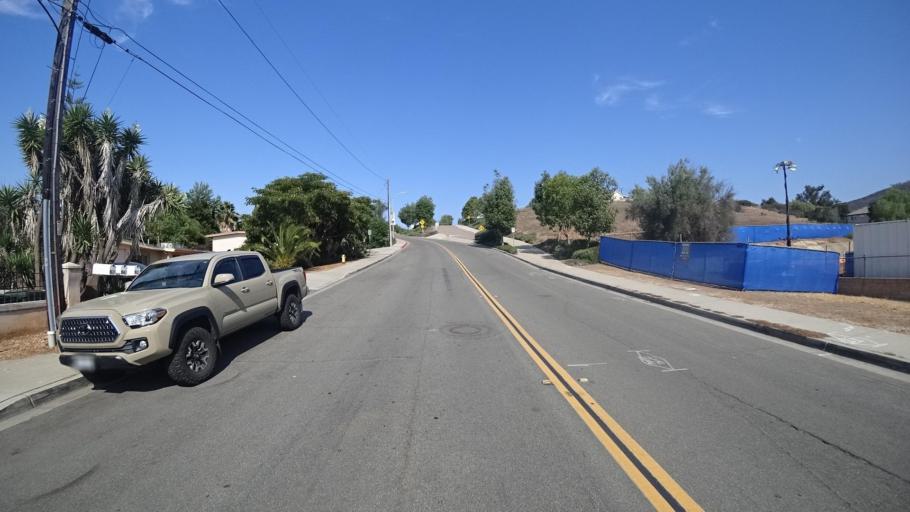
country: US
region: California
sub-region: San Diego County
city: San Marcos
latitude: 33.1551
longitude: -117.1423
